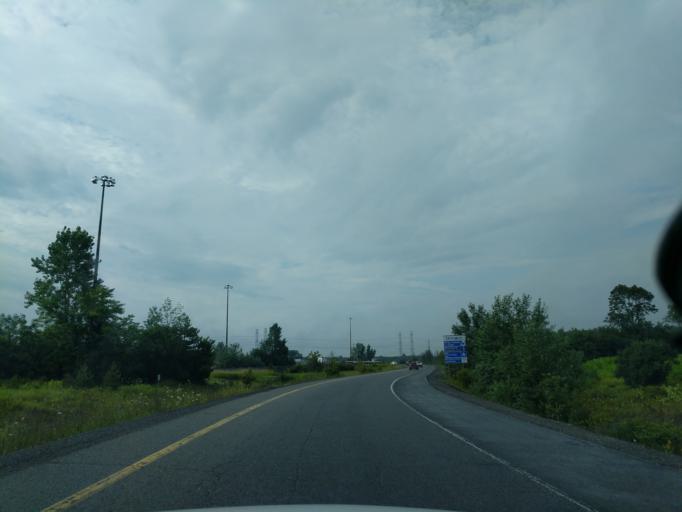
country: CA
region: Ontario
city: Bells Corners
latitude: 45.3150
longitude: -75.8043
